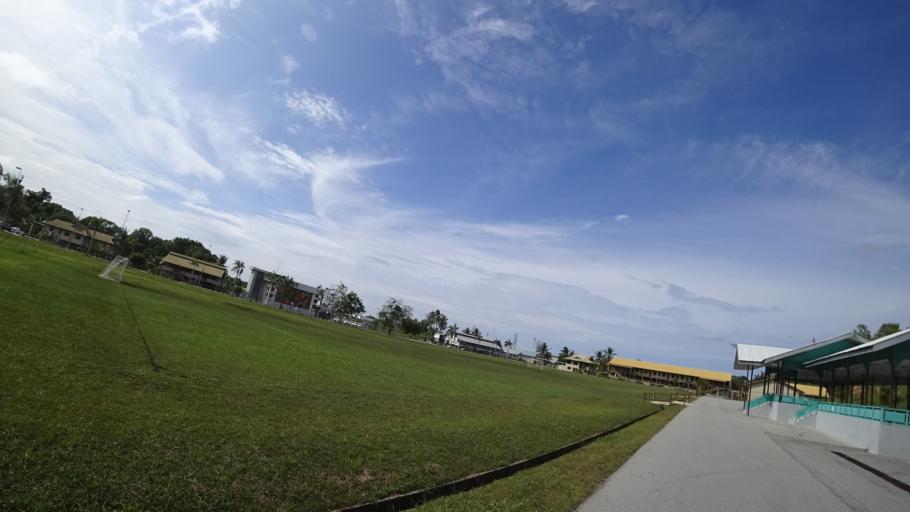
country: BN
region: Tutong
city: Tutong
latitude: 4.8072
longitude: 114.6603
